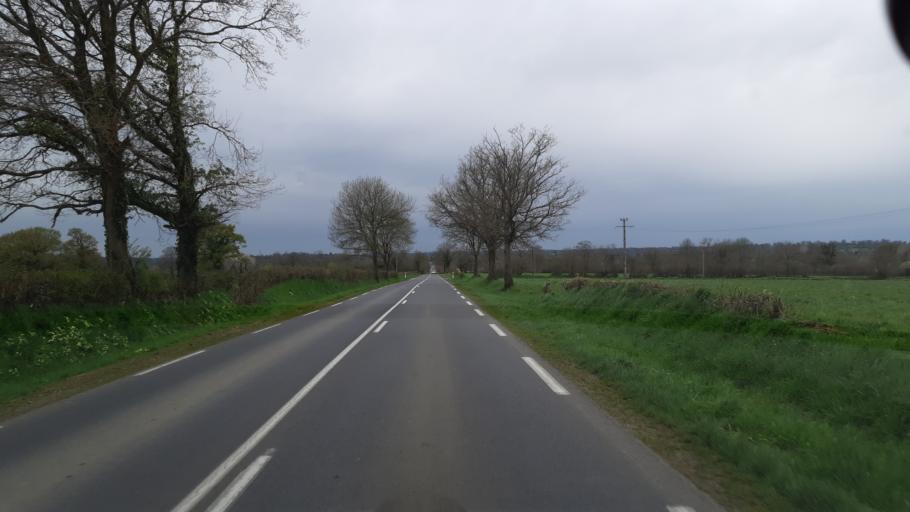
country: FR
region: Lower Normandy
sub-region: Departement de la Manche
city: Hambye
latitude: 48.9513
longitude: -1.2409
